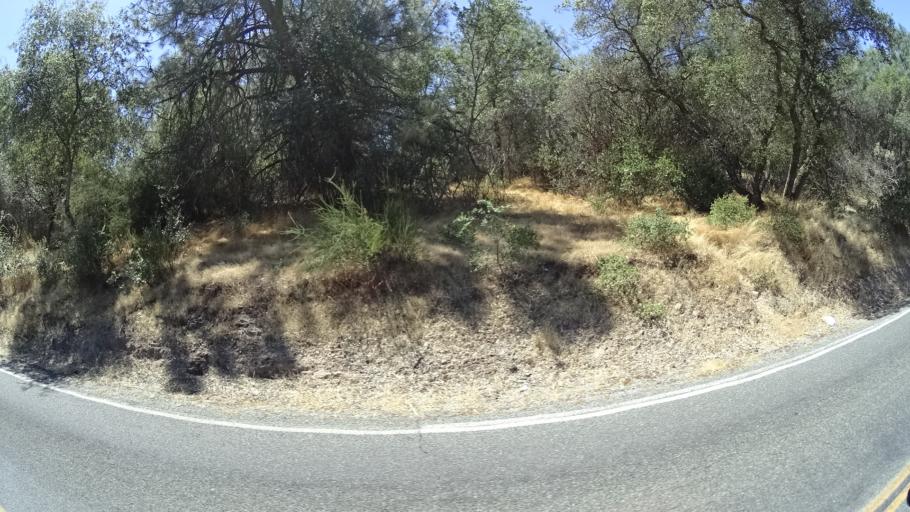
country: US
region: California
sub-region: Calaveras County
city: Valley Springs
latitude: 38.2125
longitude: -120.9106
